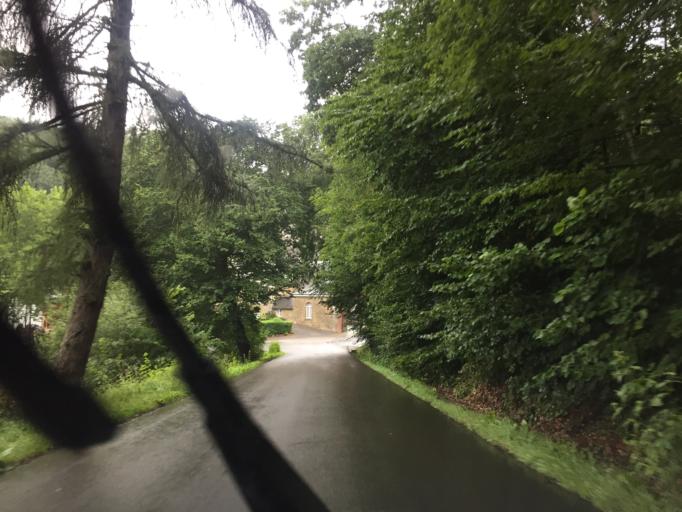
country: BE
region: Wallonia
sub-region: Province de Liege
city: Spa
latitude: 50.4950
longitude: 5.8612
